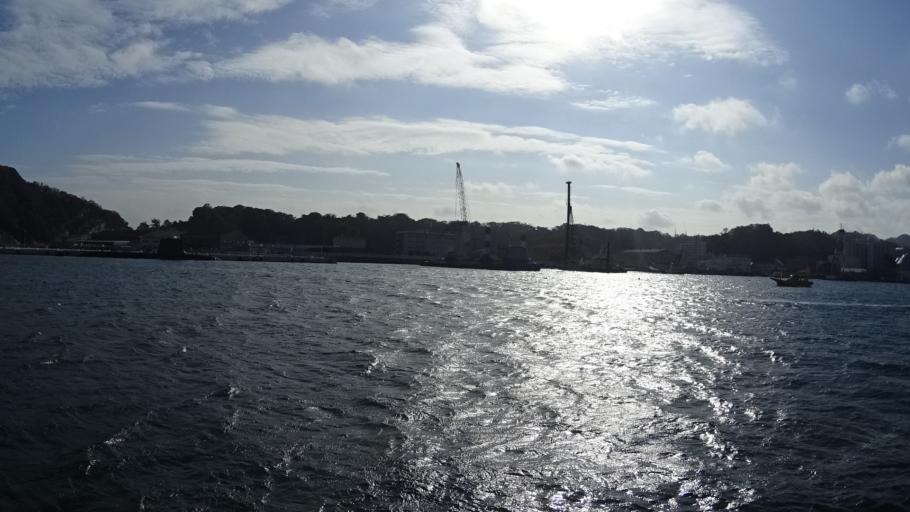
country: JP
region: Kanagawa
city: Yokosuka
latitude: 35.2993
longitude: 139.6395
